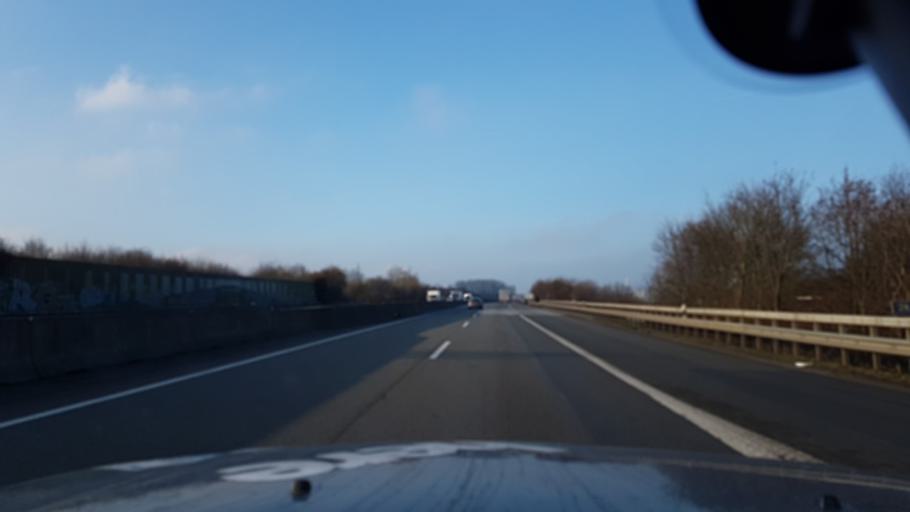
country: DE
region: North Rhine-Westphalia
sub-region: Regierungsbezirk Munster
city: Rheine
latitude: 52.3219
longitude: 7.4320
